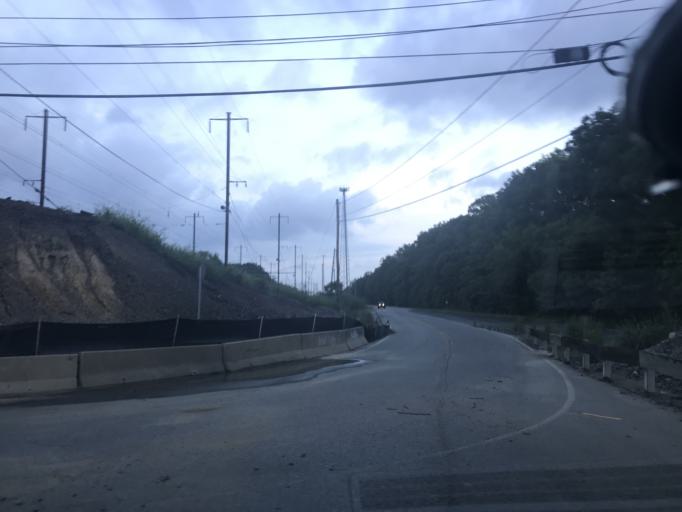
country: US
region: Maryland
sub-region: Cecil County
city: Perryville
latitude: 39.5578
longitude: -76.0733
